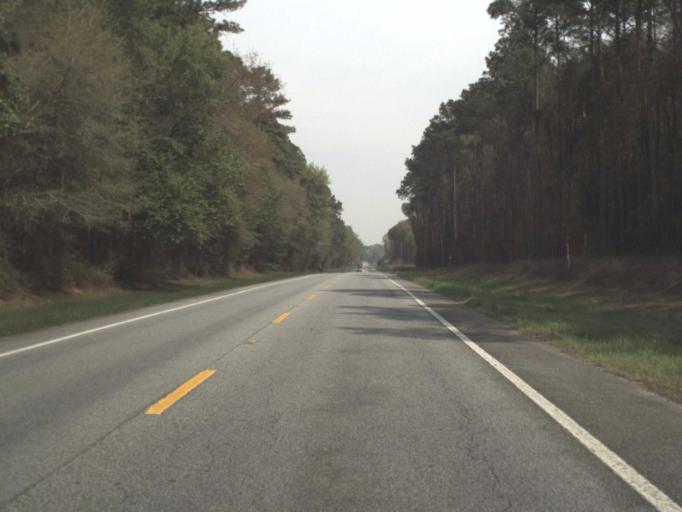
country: US
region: Florida
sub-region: Jackson County
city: Malone
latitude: 30.9760
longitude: -85.0327
